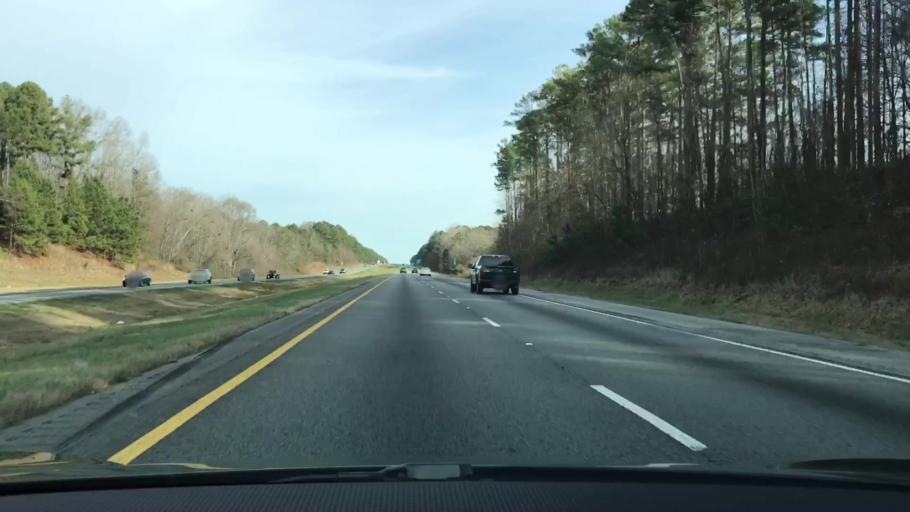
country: US
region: Georgia
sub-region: Walton County
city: Social Circle
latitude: 33.6102
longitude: -83.7821
